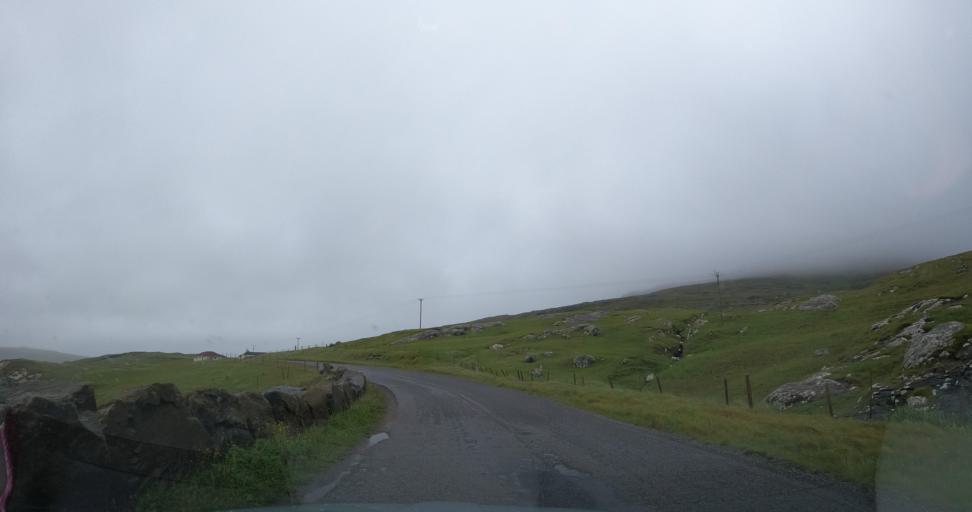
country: GB
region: Scotland
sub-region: Eilean Siar
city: Barra
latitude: 56.9920
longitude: -7.5076
